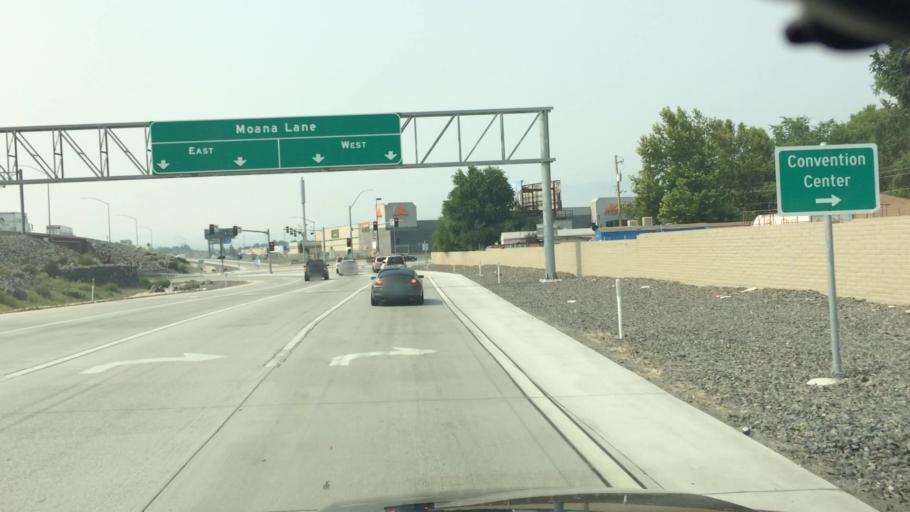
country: US
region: Nevada
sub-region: Washoe County
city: Reno
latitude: 39.4942
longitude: -119.7849
